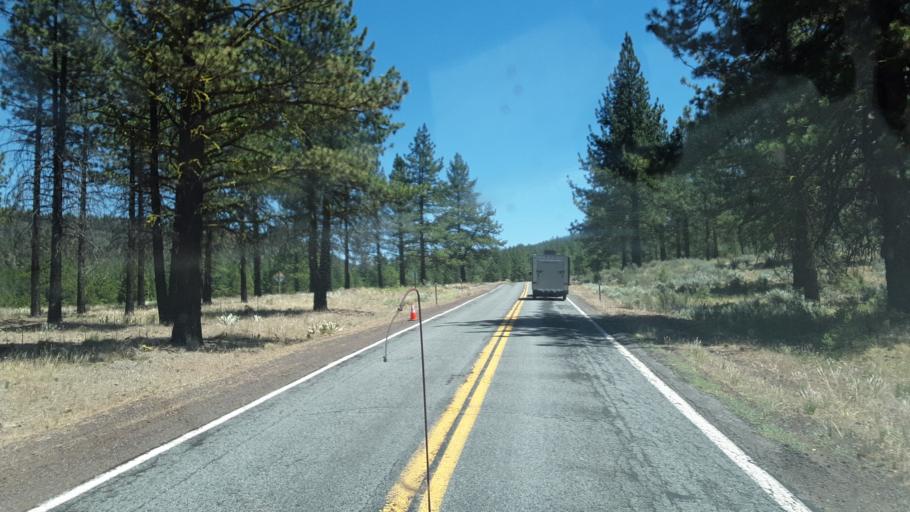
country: US
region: California
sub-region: Modoc County
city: Alturas
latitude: 40.9797
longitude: -120.7884
